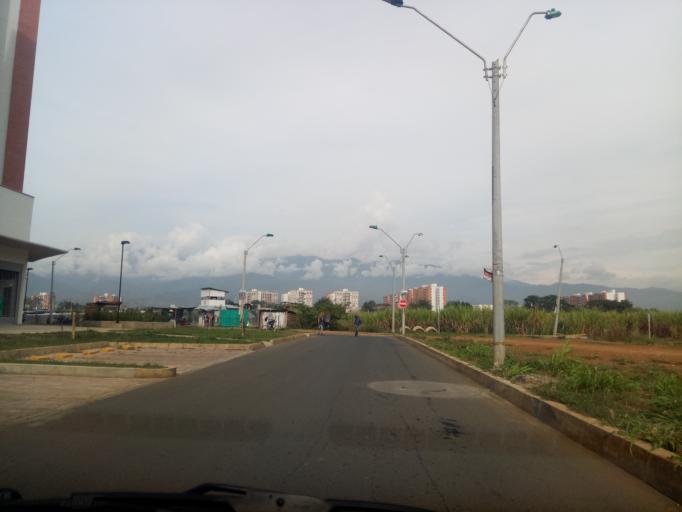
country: CO
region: Valle del Cauca
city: Cali
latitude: 3.3687
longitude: -76.5055
